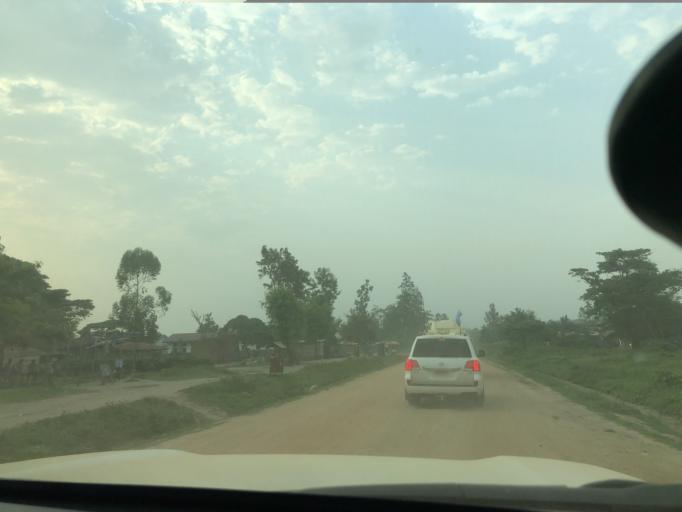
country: UG
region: Western Region
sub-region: Kasese District
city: Margherita
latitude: 0.3334
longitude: 29.6733
